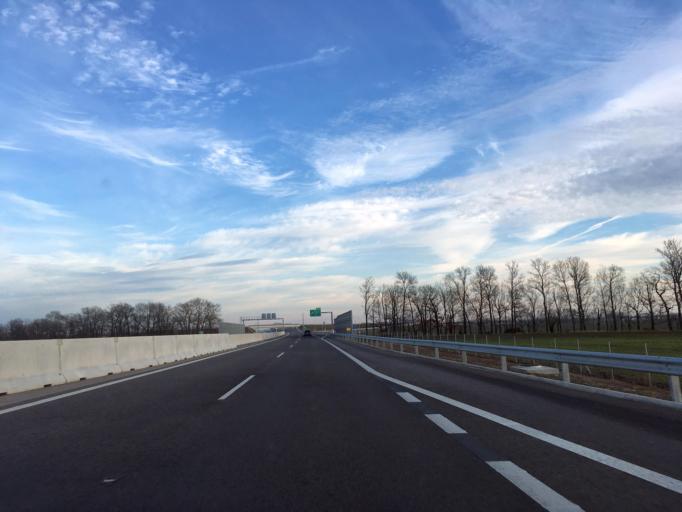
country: SK
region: Bratislavsky
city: Dunajska Luzna
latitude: 48.0634
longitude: 17.2746
